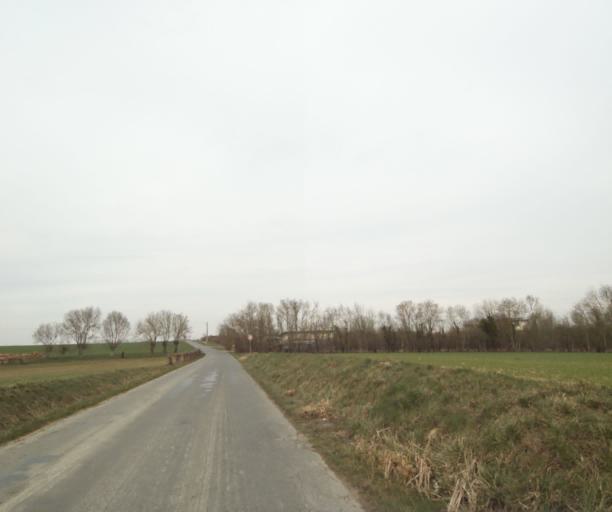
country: FR
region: Poitou-Charentes
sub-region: Departement des Deux-Sevres
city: Bessines
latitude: 46.3096
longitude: -0.5168
